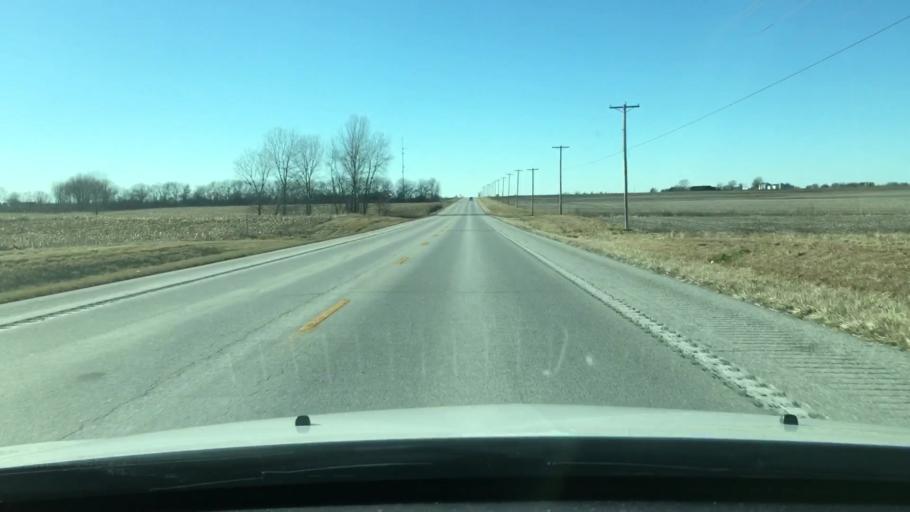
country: US
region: Missouri
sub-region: Pike County
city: Bowling Green
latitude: 39.3445
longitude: -91.2849
